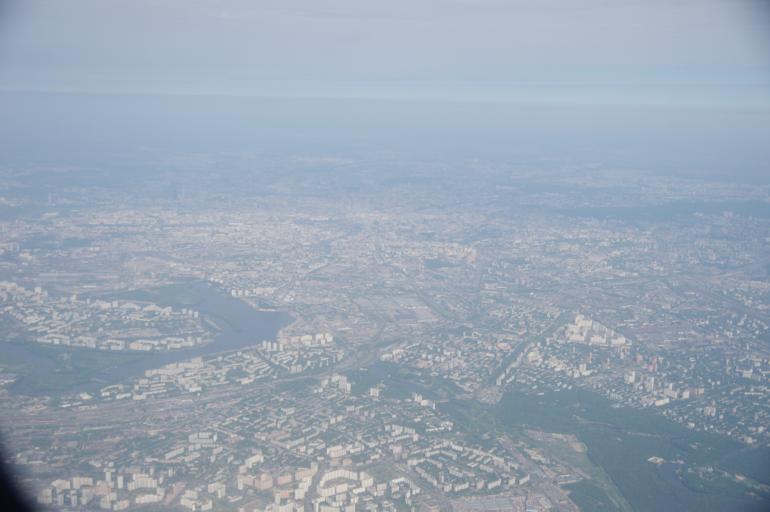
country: RU
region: Moskovskaya
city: Kotel'niki
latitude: 55.6351
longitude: 37.8265
